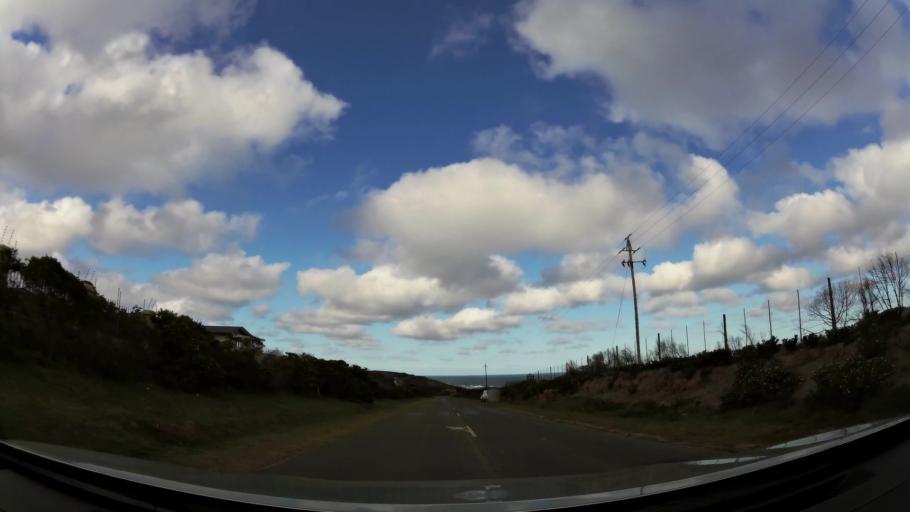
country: ZA
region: Western Cape
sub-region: Eden District Municipality
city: Plettenberg Bay
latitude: -34.0964
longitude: 23.3664
